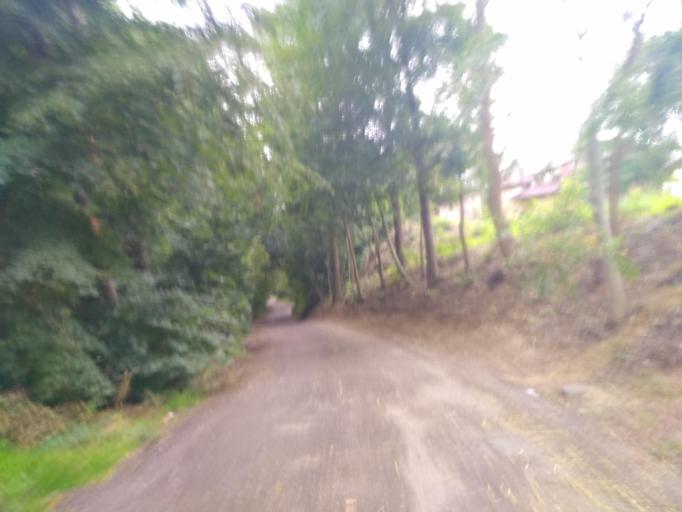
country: PL
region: Subcarpathian Voivodeship
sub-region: Powiat rzeszowski
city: Tyczyn
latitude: 49.9632
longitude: 21.9981
